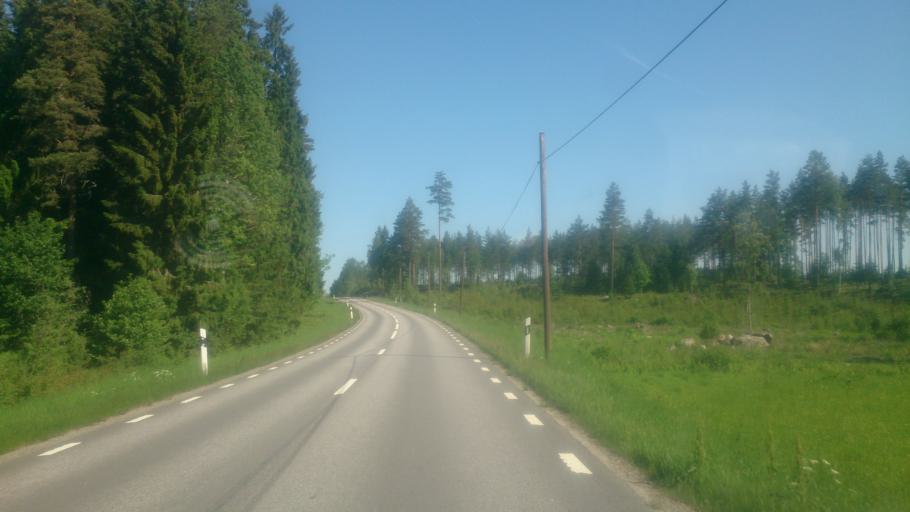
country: SE
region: OEstergoetland
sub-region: Atvidabergs Kommun
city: Atvidaberg
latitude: 58.1317
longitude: 16.0927
